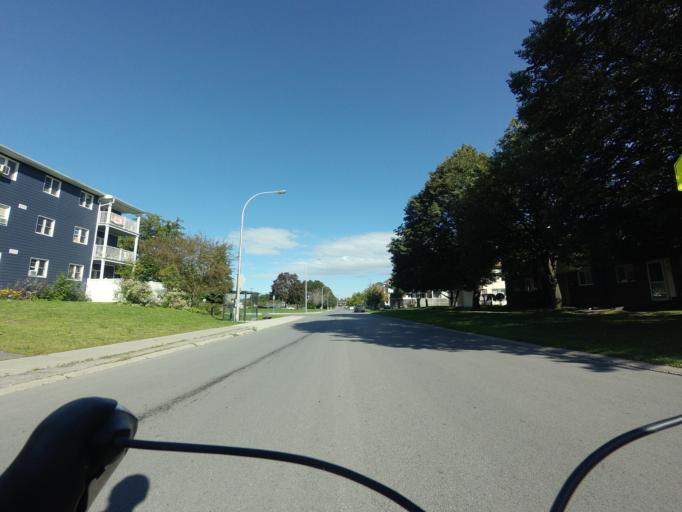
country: CA
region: Ontario
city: Bells Corners
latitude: 45.3135
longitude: -75.8314
